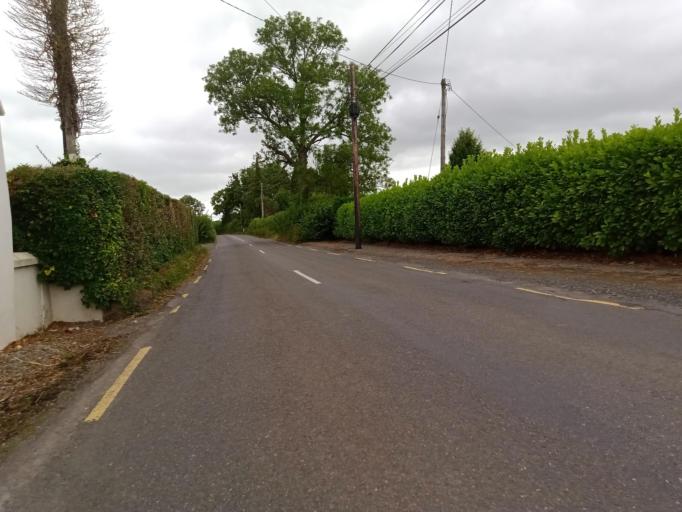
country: IE
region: Leinster
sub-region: Kilkenny
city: Callan
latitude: 52.5655
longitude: -7.4135
